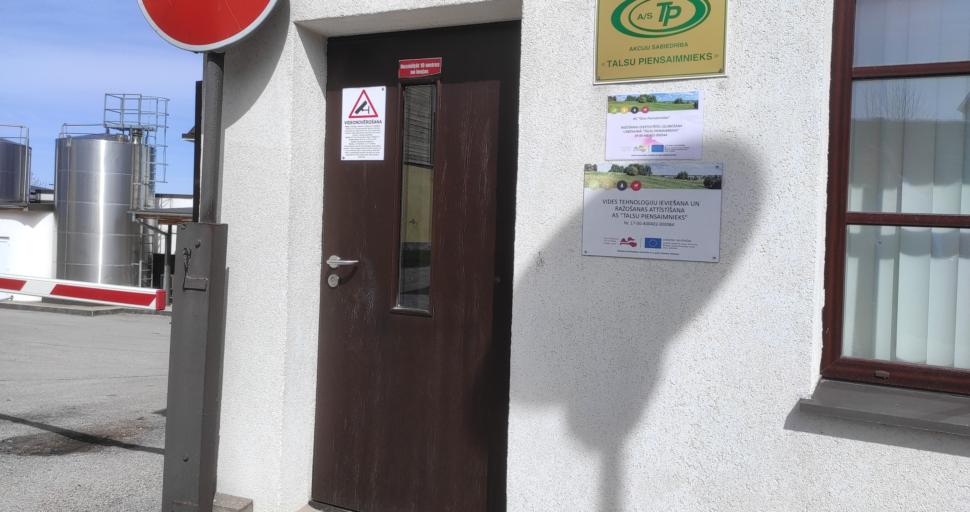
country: LV
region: Talsu Rajons
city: Talsi
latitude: 57.2457
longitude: 22.5961
